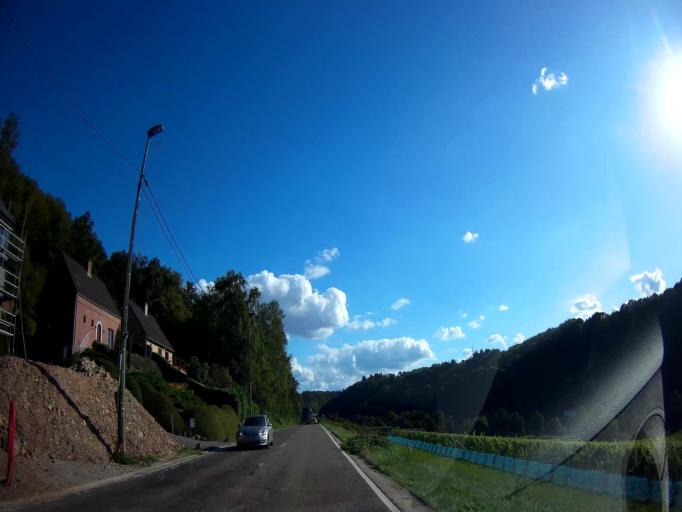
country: BE
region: Wallonia
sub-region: Province de Namur
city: Dinant
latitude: 50.2835
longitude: 4.8967
